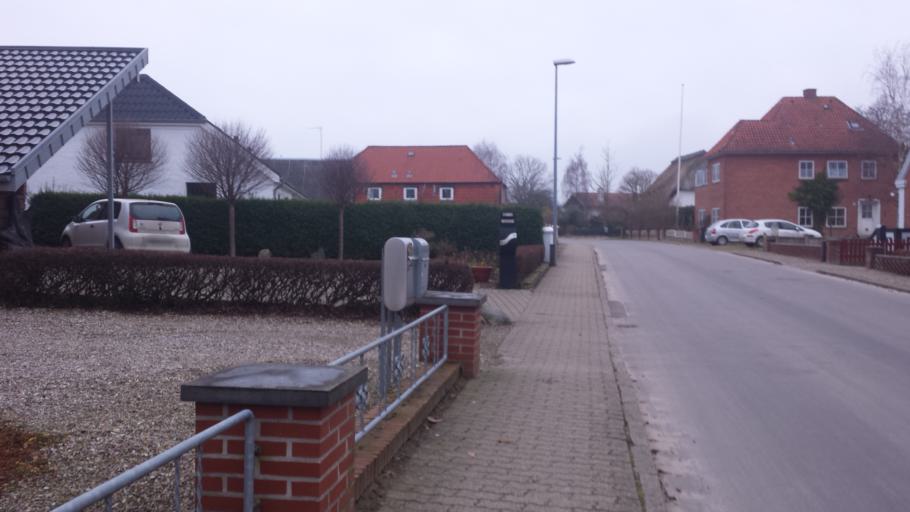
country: DK
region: South Denmark
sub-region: Sonderborg Kommune
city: Grasten
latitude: 54.9075
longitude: 9.5889
